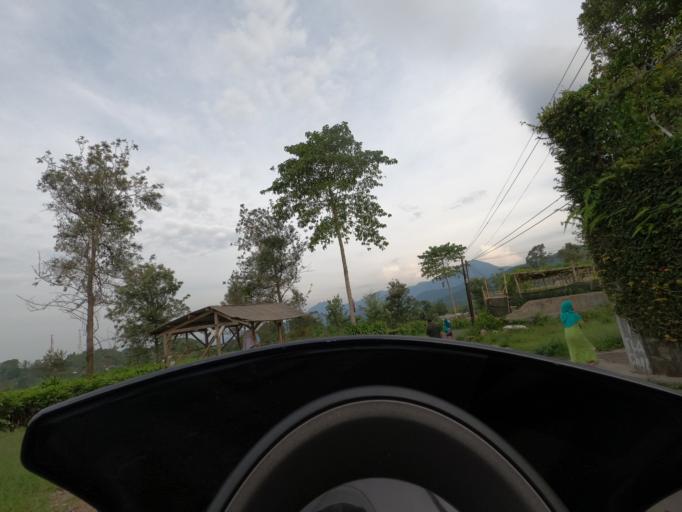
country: ID
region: West Java
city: Lembang
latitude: -6.7320
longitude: 107.6493
